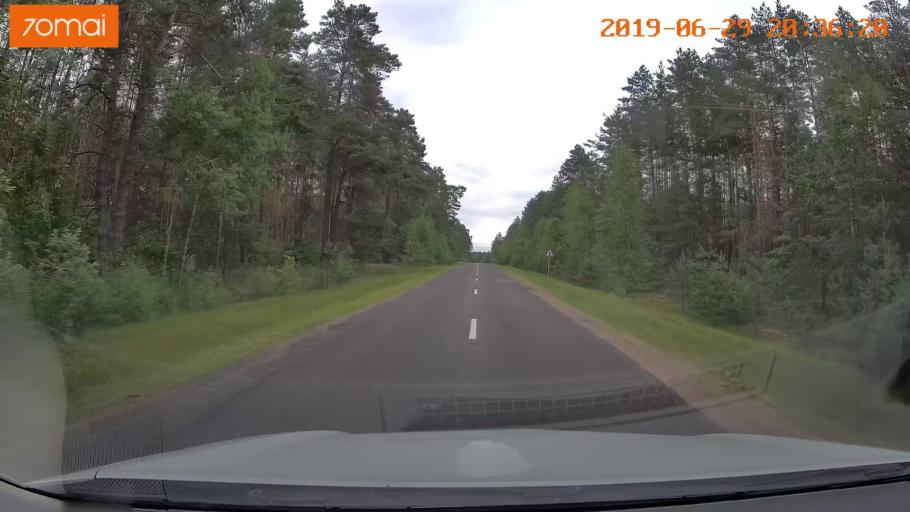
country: BY
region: Brest
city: Hantsavichy
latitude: 52.5251
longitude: 26.3577
